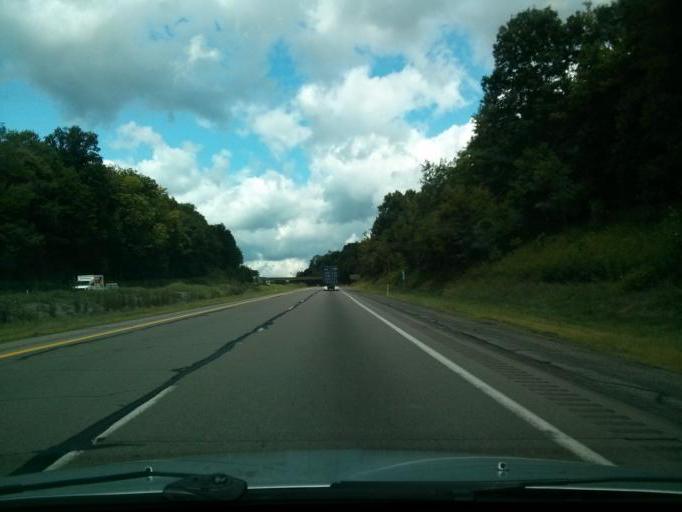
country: US
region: Pennsylvania
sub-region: Jefferson County
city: Brookville
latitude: 41.1665
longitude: -79.0085
